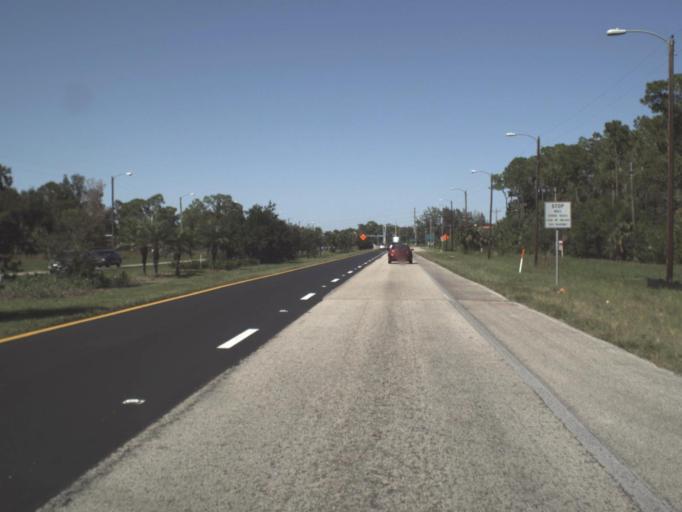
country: US
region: Florida
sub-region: Lee County
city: Palmona Park
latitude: 26.7204
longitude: -81.9048
